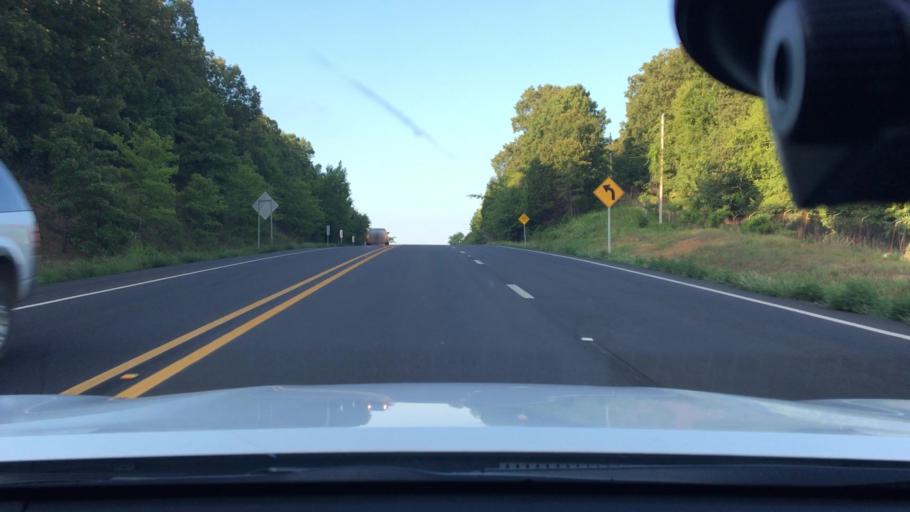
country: US
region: Arkansas
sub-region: Johnson County
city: Clarksville
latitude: 35.4203
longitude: -93.5311
